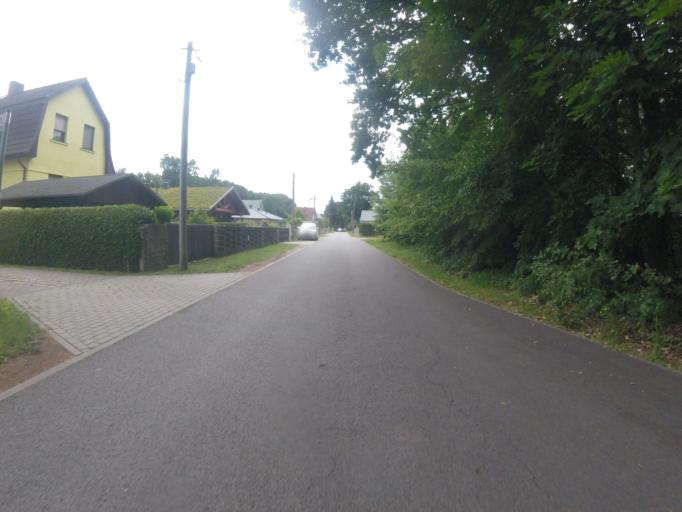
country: DE
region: Brandenburg
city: Bestensee
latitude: 52.2395
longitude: 13.6443
